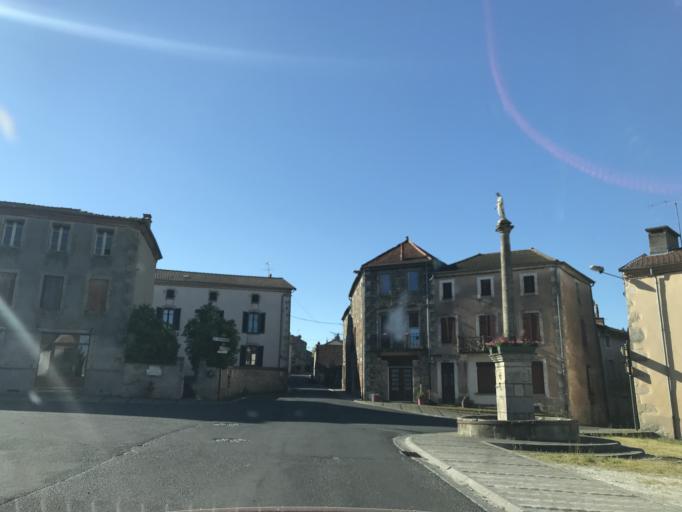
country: FR
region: Auvergne
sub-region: Departement du Puy-de-Dome
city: Job
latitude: 45.6183
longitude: 3.6807
